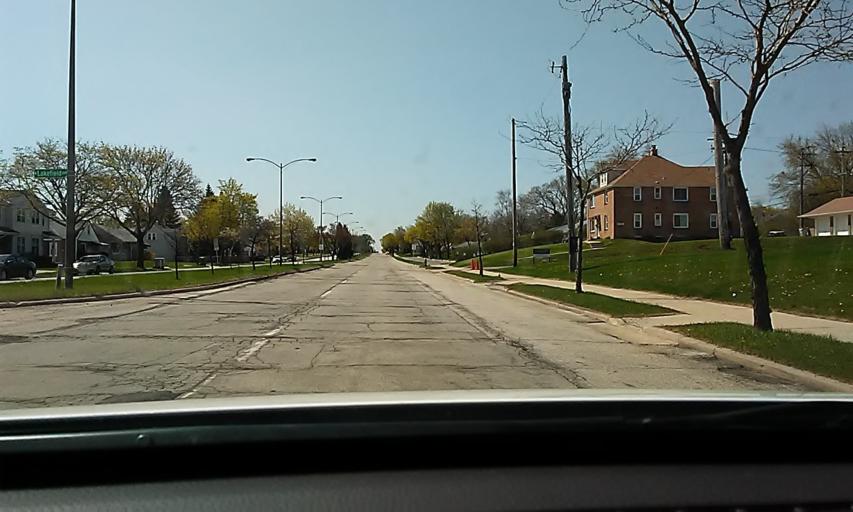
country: US
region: Wisconsin
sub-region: Milwaukee County
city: West Milwaukee
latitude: 42.9874
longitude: -87.9879
